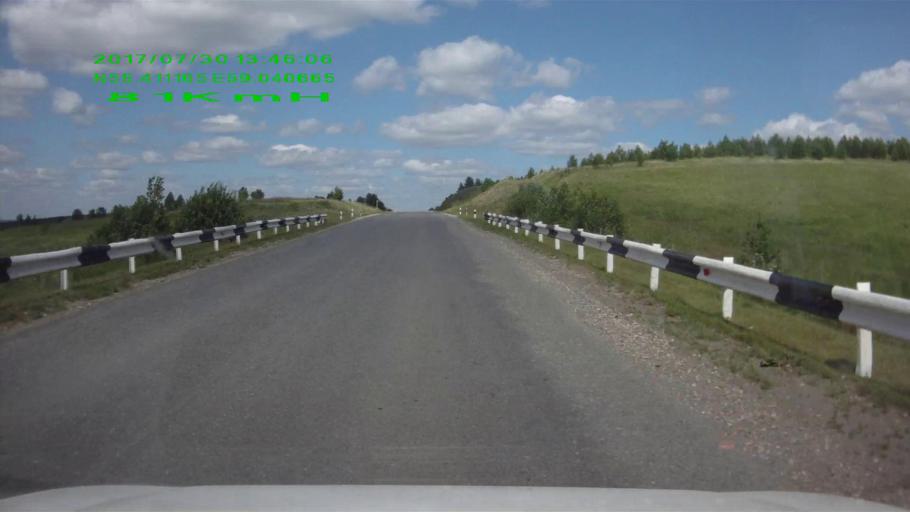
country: RU
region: Sverdlovsk
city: Mikhaylovsk
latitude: 56.4115
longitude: 59.0407
